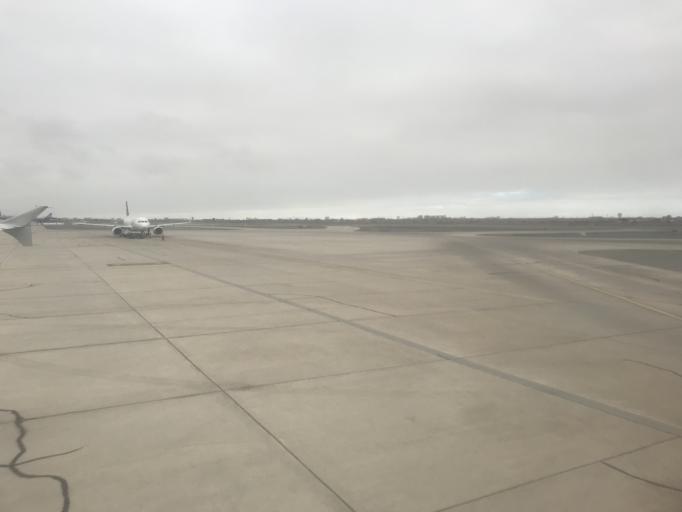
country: PE
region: Callao
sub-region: Callao
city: Callao
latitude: -12.0225
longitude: -77.1106
